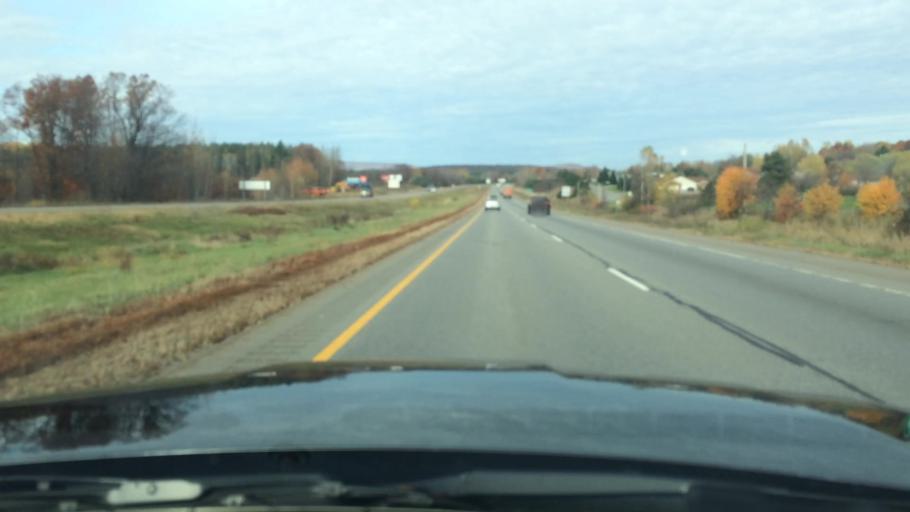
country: US
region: Wisconsin
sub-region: Marathon County
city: Mosinee
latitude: 44.7943
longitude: -89.6796
